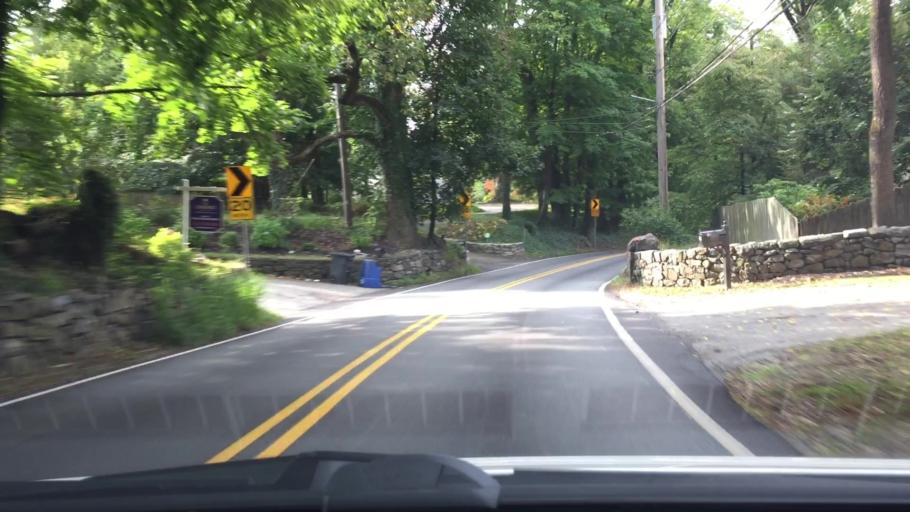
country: US
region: Pennsylvania
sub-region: Delaware County
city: Radnor
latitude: 40.0329
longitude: -75.3662
